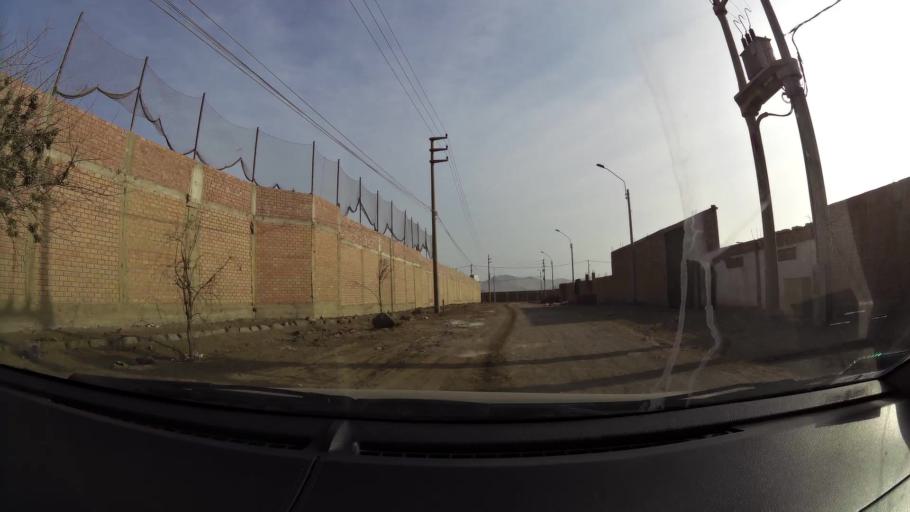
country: PE
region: Lima
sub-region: Lima
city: Santa Rosa
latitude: -11.7547
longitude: -77.1578
